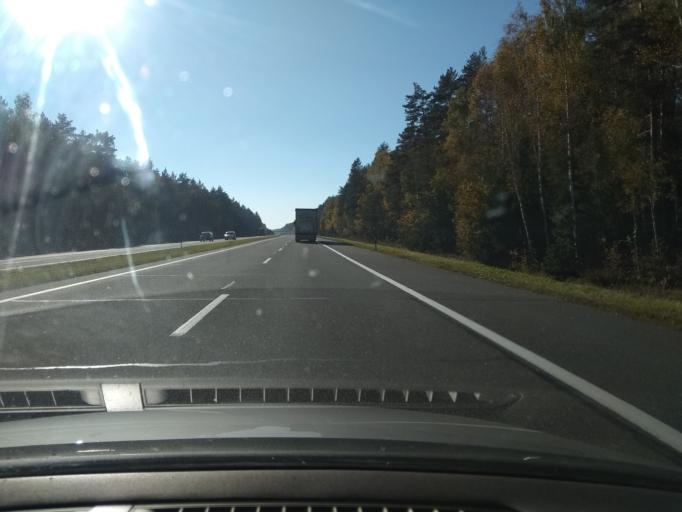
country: BY
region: Brest
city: Baranovichi
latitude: 53.0415
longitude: 25.8279
